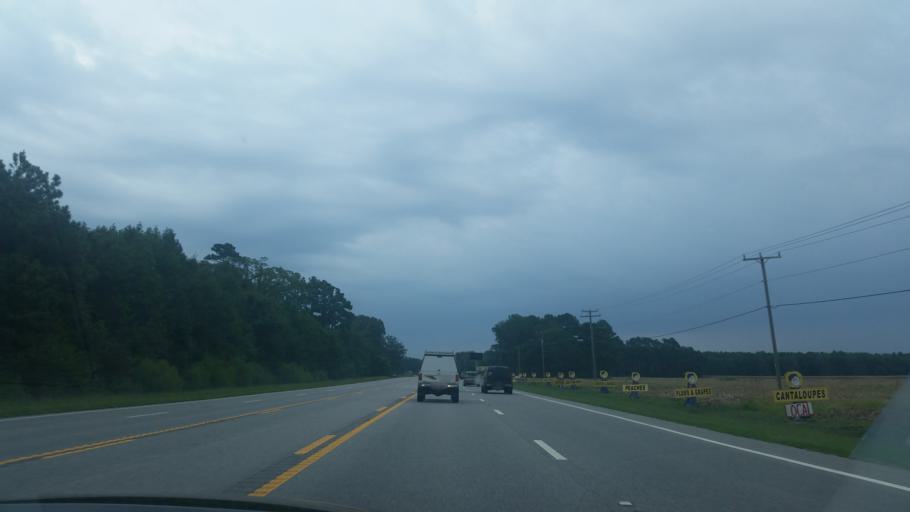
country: US
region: North Carolina
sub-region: Currituck County
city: Currituck
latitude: 36.4572
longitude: -76.0919
